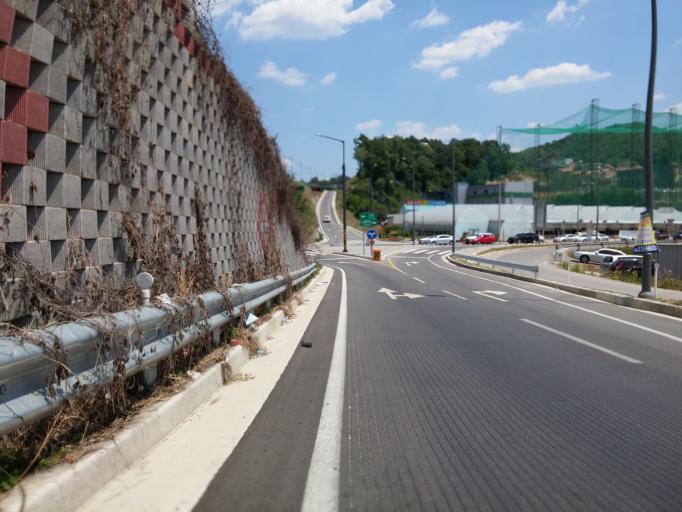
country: KR
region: Chungcheongbuk-do
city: Cheongju-si
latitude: 36.6028
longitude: 127.4397
